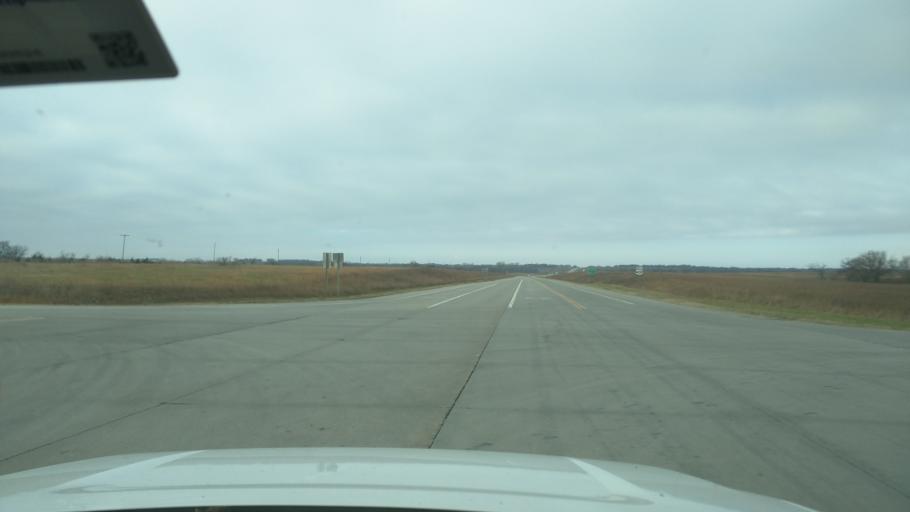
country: US
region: Kansas
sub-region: Elk County
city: Howard
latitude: 37.6365
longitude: -96.2528
